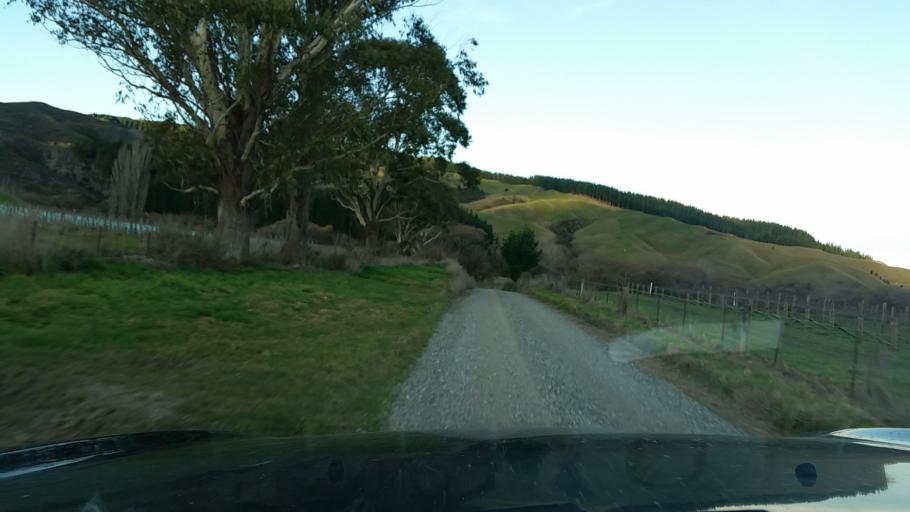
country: NZ
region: Marlborough
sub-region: Marlborough District
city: Blenheim
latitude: -41.5138
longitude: 173.5886
